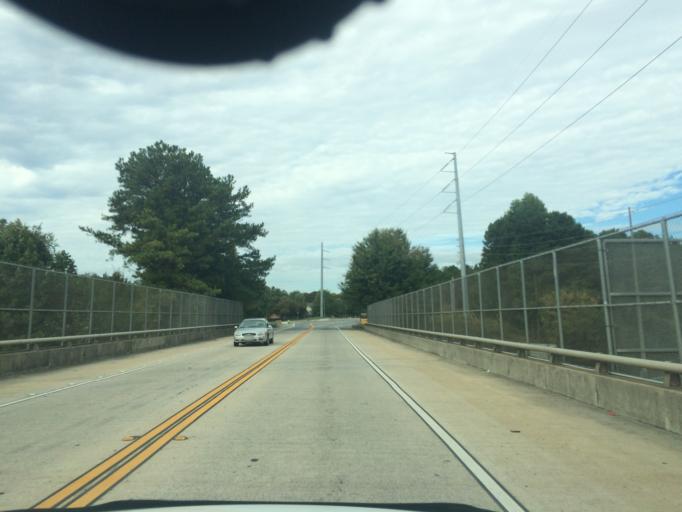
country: US
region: Georgia
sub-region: Cobb County
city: Kennesaw
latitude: 34.0491
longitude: -84.5861
